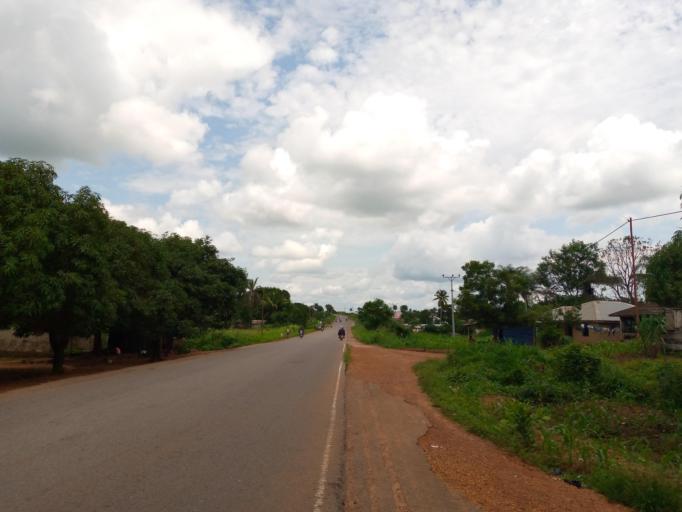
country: SL
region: Northern Province
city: Magburaka
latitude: 8.7095
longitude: -11.9264
